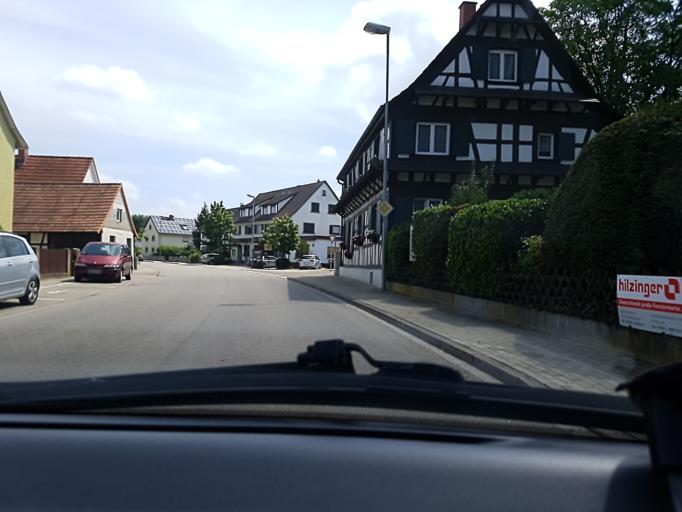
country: DE
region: Baden-Wuerttemberg
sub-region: Freiburg Region
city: Kehl
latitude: 48.5690
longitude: 7.8461
